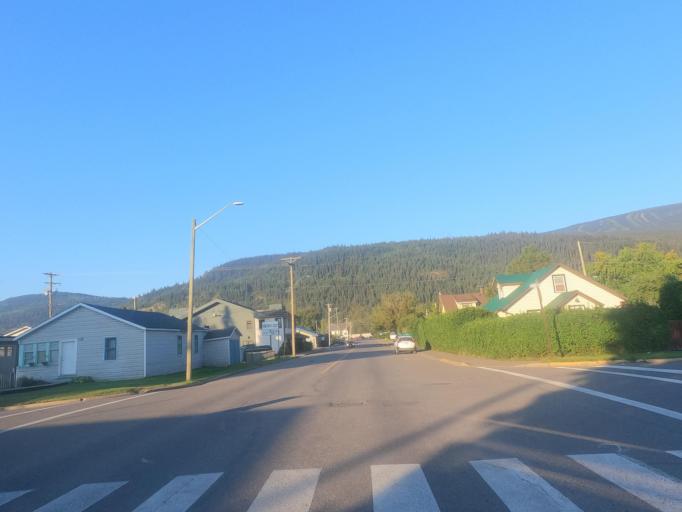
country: CA
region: British Columbia
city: Smithers
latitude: 54.7817
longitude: -127.1725
